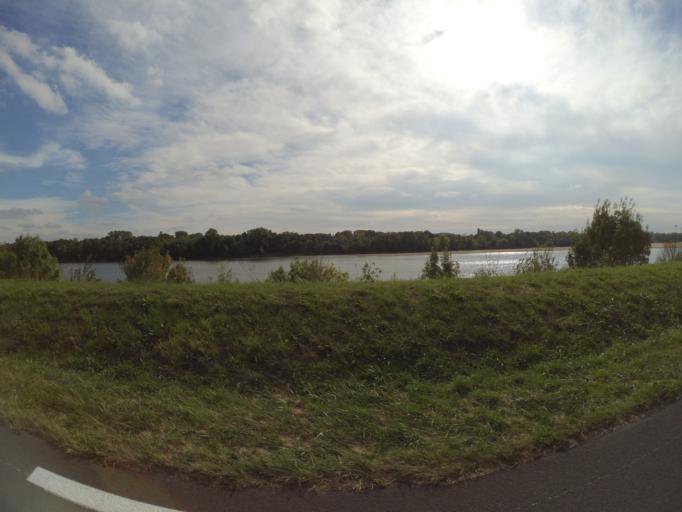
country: FR
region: Centre
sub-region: Departement d'Indre-et-Loire
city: Huismes
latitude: 47.2585
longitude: 0.2551
